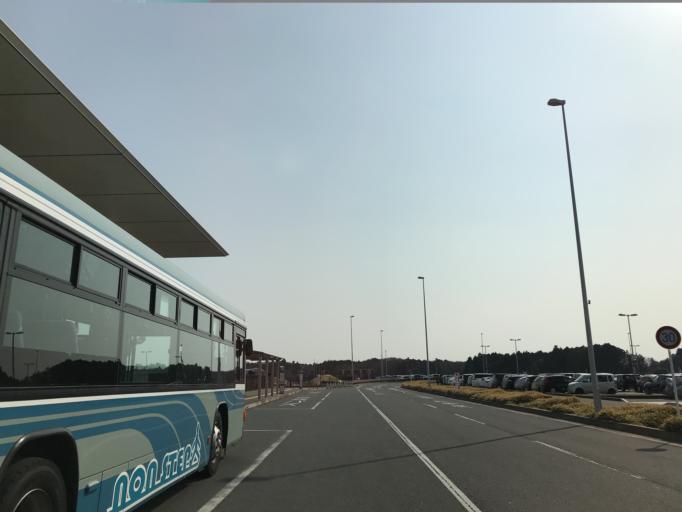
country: JP
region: Ibaraki
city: Okunoya
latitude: 36.1777
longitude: 140.4071
